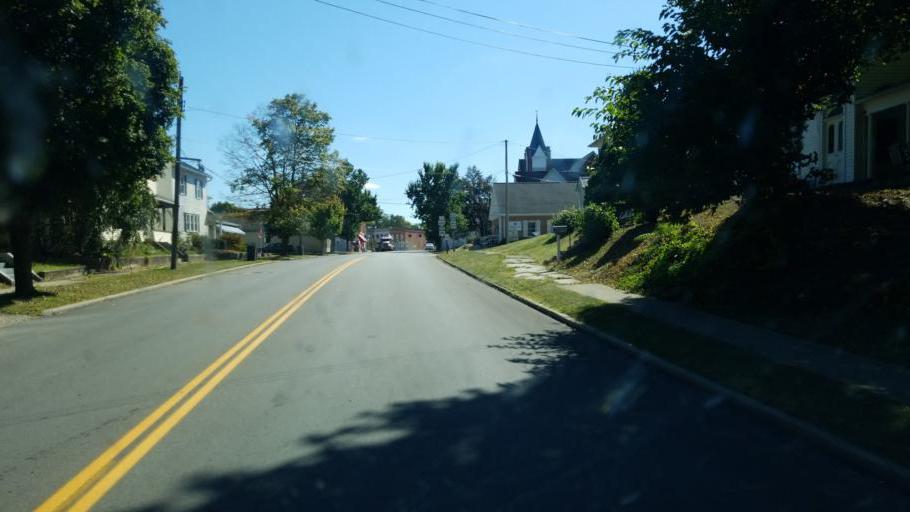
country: US
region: Ohio
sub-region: Huron County
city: Plymouth
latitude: 40.9972
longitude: -82.6664
